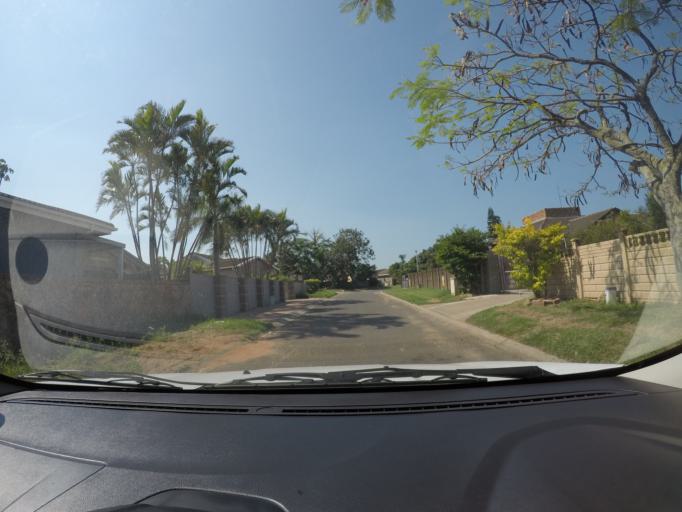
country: ZA
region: KwaZulu-Natal
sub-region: uThungulu District Municipality
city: Richards Bay
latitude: -28.7237
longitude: 32.0463
